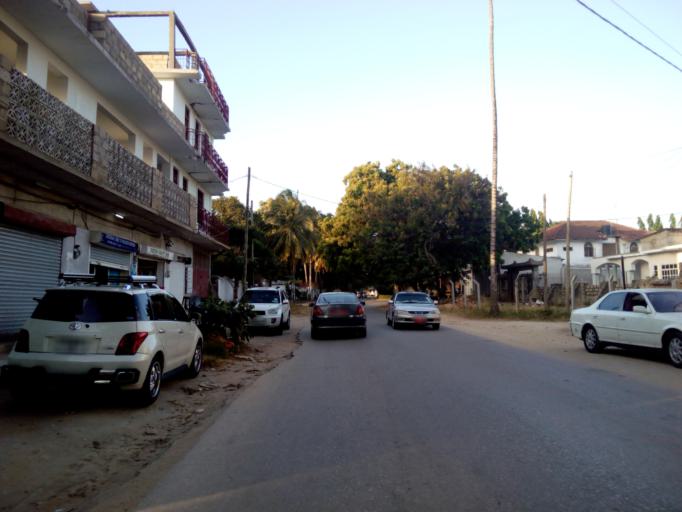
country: TZ
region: Zanzibar Urban/West
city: Zanzibar
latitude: -6.2034
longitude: 39.2102
